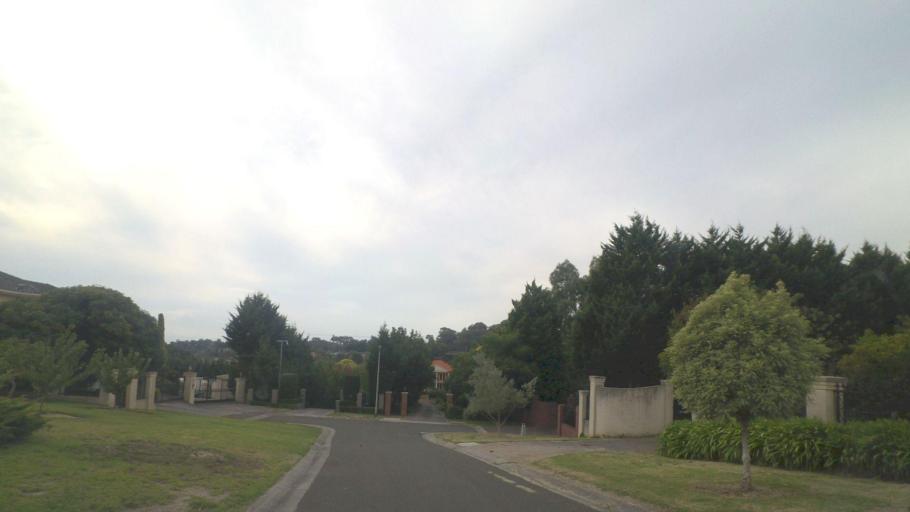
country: AU
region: Victoria
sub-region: Manningham
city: Park Orchards
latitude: -37.7661
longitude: 145.1956
